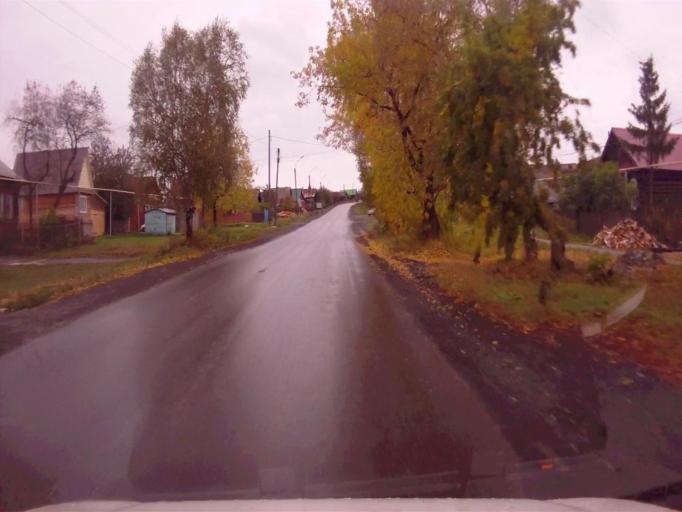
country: RU
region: Chelyabinsk
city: Verkhniy Ufaley
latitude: 56.0502
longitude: 60.2061
